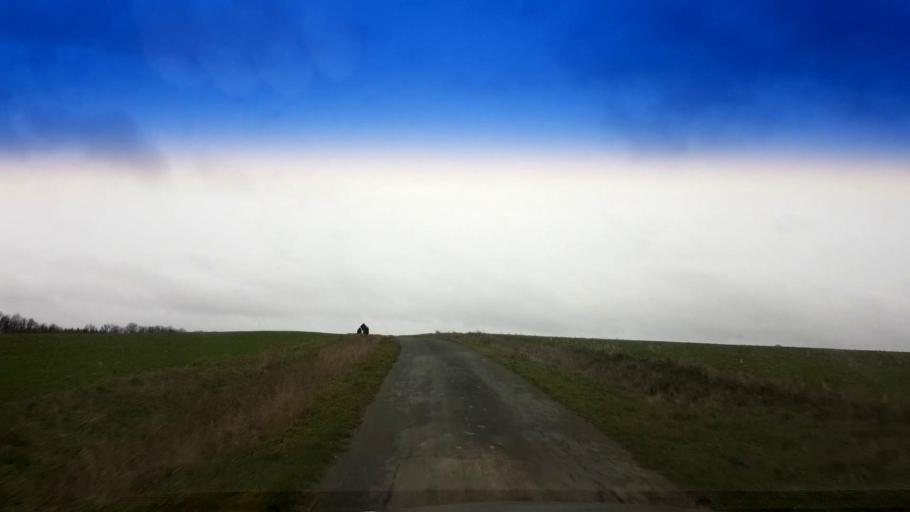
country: DE
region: Bavaria
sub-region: Upper Franconia
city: Rattelsdorf
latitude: 50.0664
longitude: 10.8954
